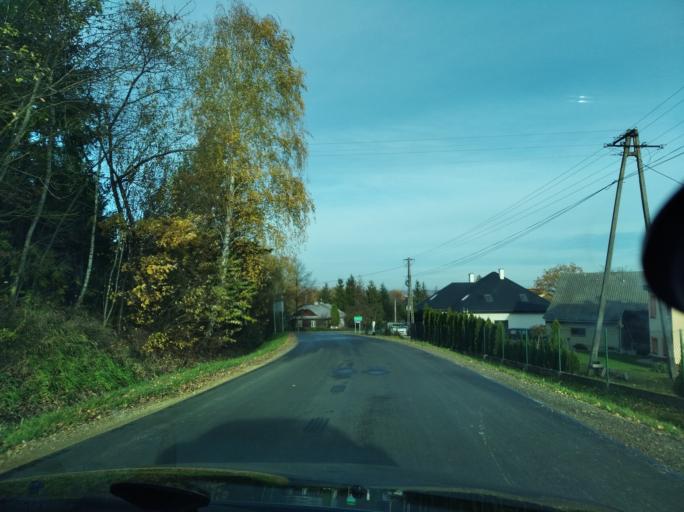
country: PL
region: Subcarpathian Voivodeship
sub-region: Powiat rzeszowski
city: Straszydle
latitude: 49.9359
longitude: 21.9809
